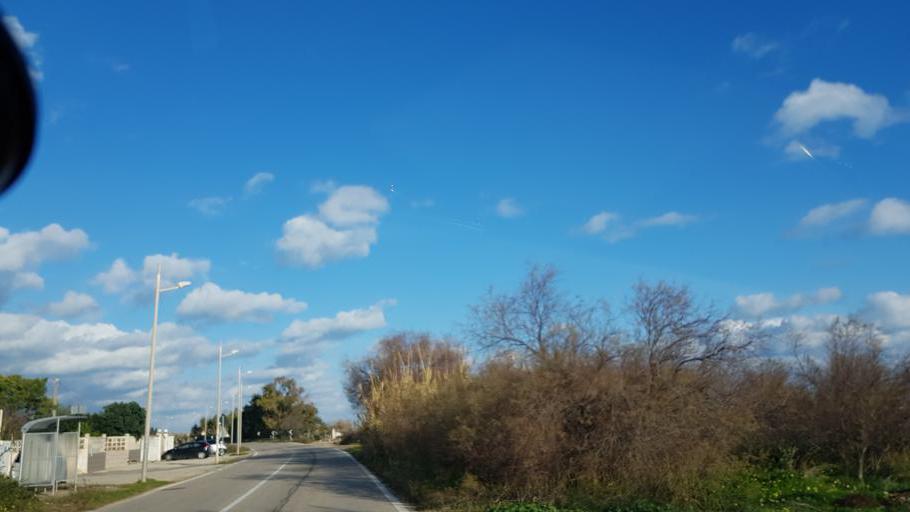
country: IT
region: Apulia
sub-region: Provincia di Brindisi
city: Materdomini
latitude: 40.6737
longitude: 17.9453
